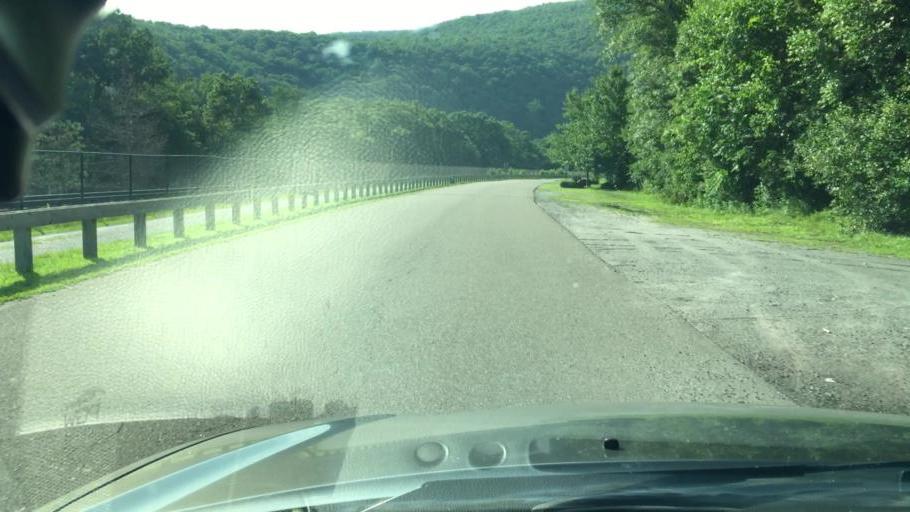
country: US
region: Pennsylvania
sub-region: Carbon County
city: Jim Thorpe
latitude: 40.8771
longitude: -75.7599
